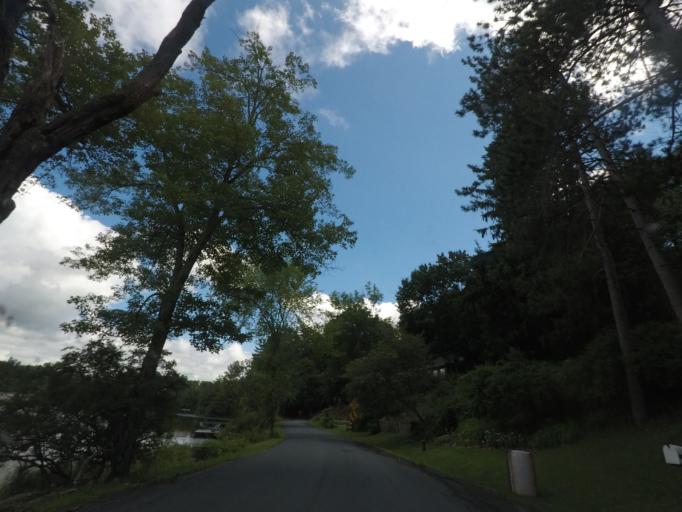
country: US
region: New York
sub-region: Rensselaer County
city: West Sand Lake
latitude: 42.6522
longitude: -73.5965
